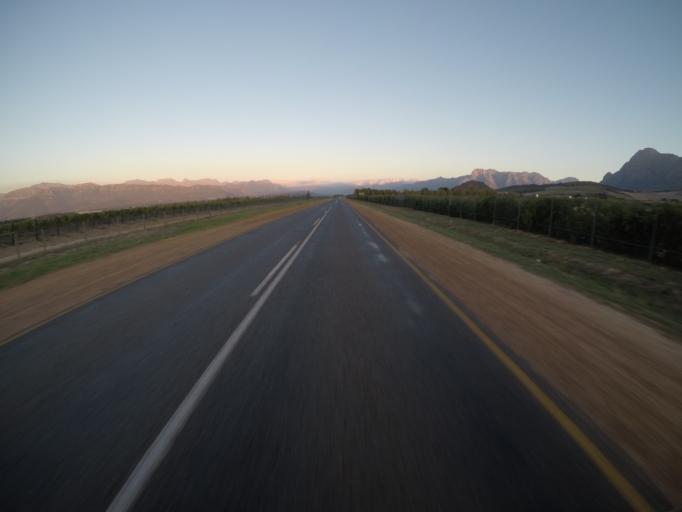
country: ZA
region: Western Cape
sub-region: Cape Winelands District Municipality
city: Paarl
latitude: -33.8192
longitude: 18.9240
